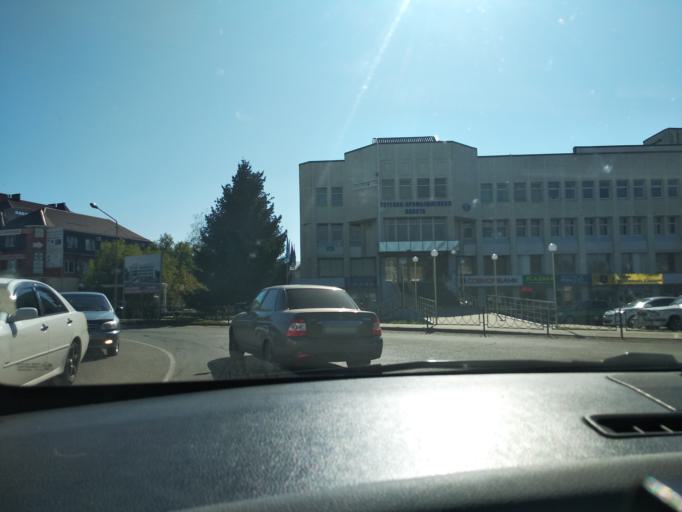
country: RU
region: Krasnodarskiy
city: Goryachiy Klyuch
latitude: 44.6340
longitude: 39.1358
